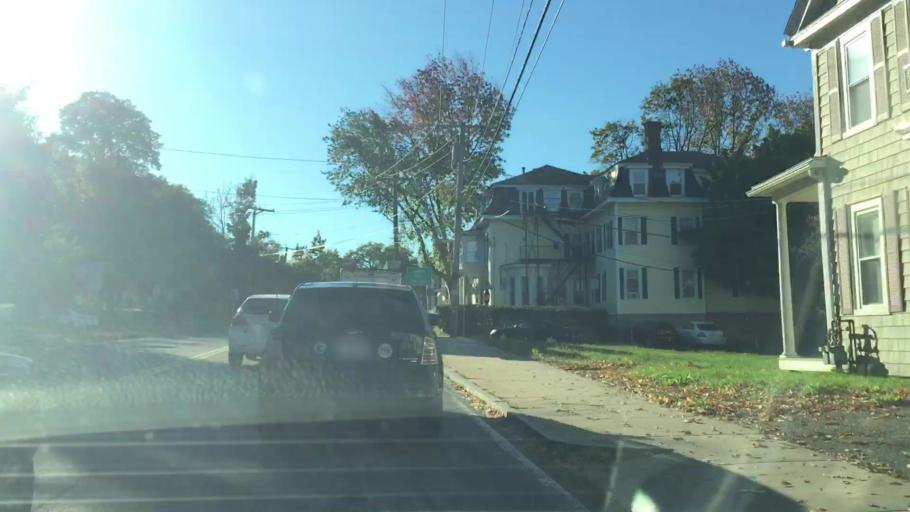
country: US
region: Massachusetts
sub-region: Middlesex County
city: Lowell
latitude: 42.6436
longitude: -71.2987
